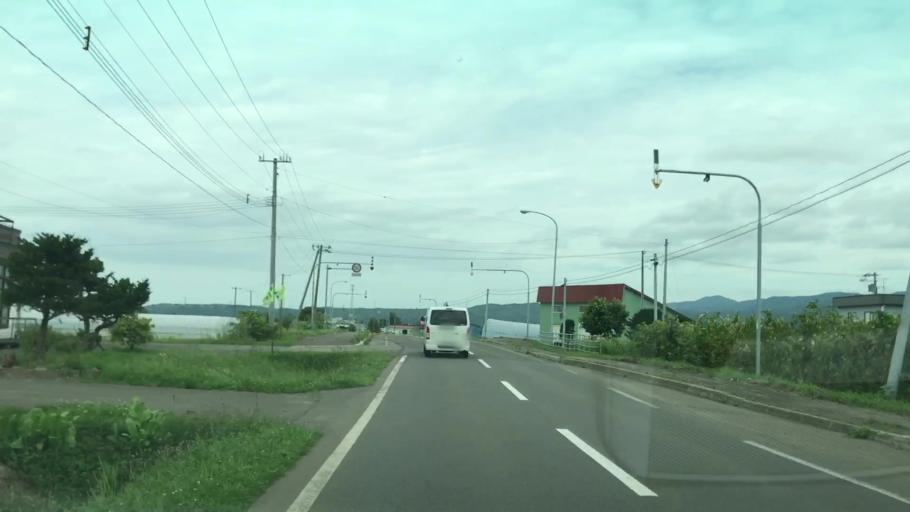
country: JP
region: Hokkaido
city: Iwanai
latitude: 43.0106
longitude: 140.5762
